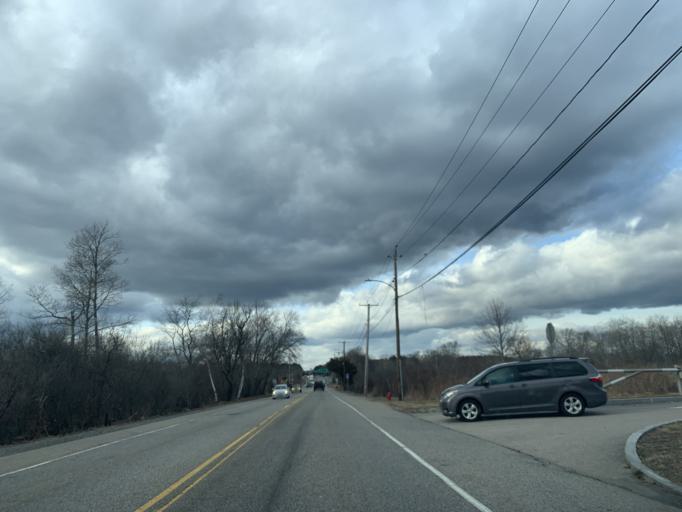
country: US
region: Massachusetts
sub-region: Norfolk County
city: Canton
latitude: 42.1663
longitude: -71.1645
